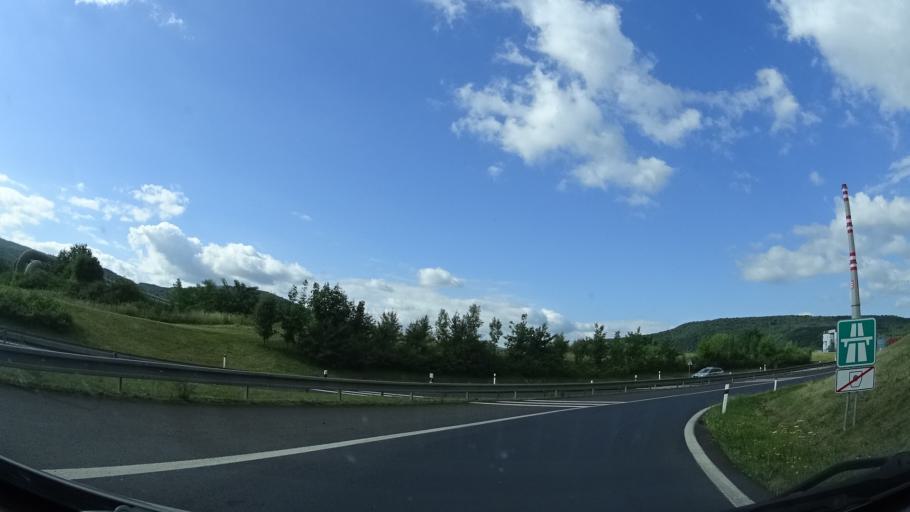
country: CZ
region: Ustecky
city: Trmice
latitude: 50.6481
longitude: 13.9960
